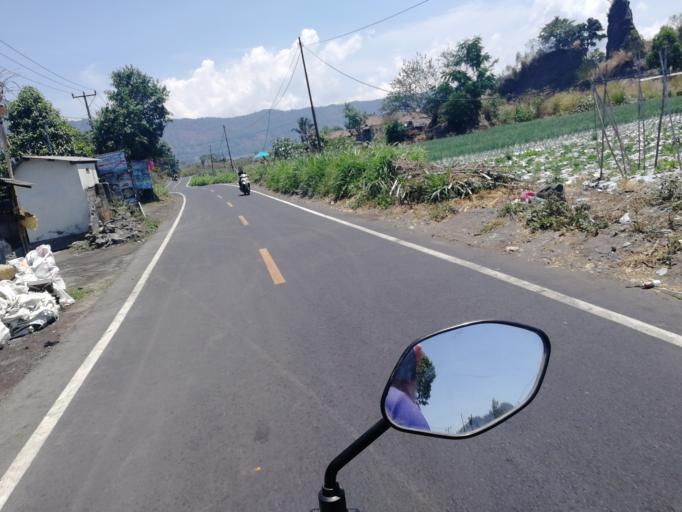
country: ID
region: Bali
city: Banjar Trunyan
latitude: -8.2387
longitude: 115.4065
